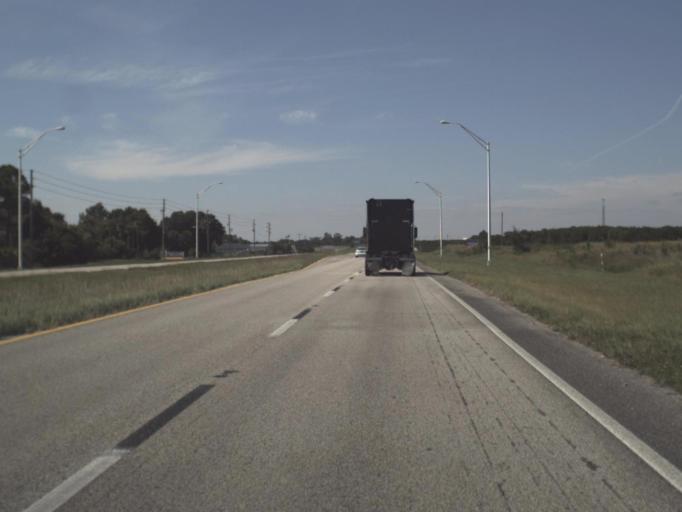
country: US
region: Florida
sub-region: Highlands County
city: Lake Placid
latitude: 27.3244
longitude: -81.3726
